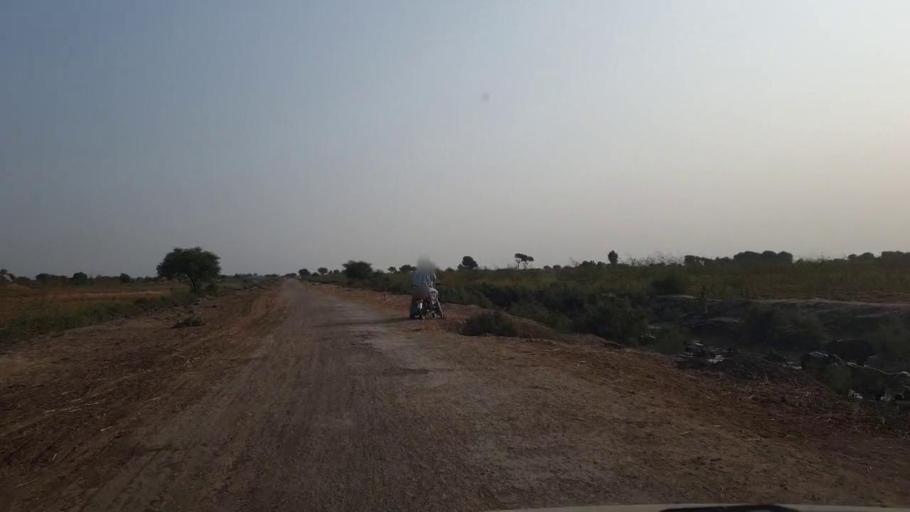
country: PK
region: Sindh
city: Matli
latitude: 25.0591
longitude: 68.7618
